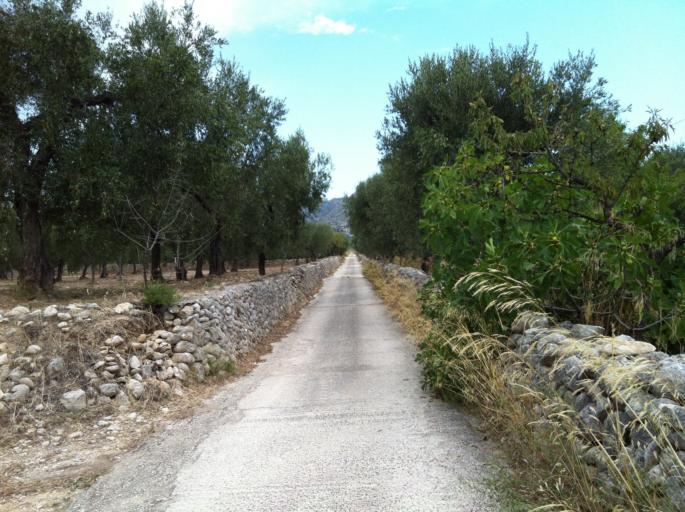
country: IT
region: Apulia
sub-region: Provincia di Foggia
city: Monte Sant'Angelo
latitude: 41.6534
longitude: 15.9563
